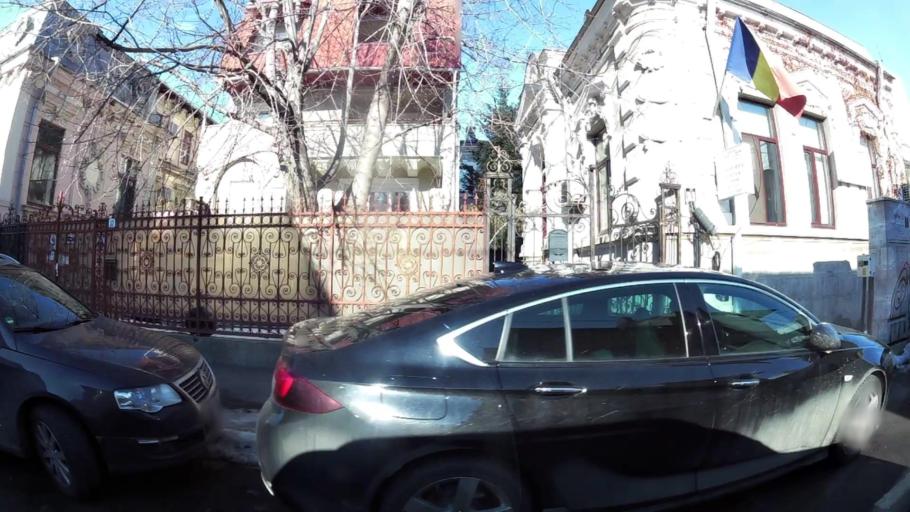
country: RO
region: Bucuresti
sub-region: Municipiul Bucuresti
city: Bucharest
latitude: 44.4514
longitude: 26.0922
